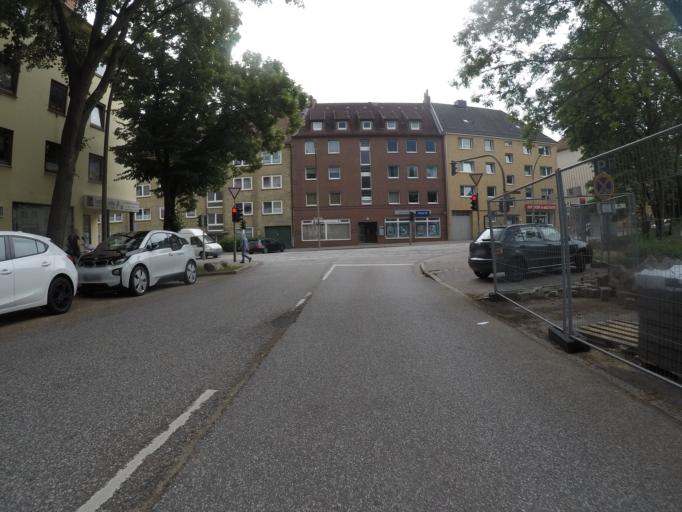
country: DE
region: Hamburg
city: Harburg
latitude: 53.4599
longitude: 9.9718
